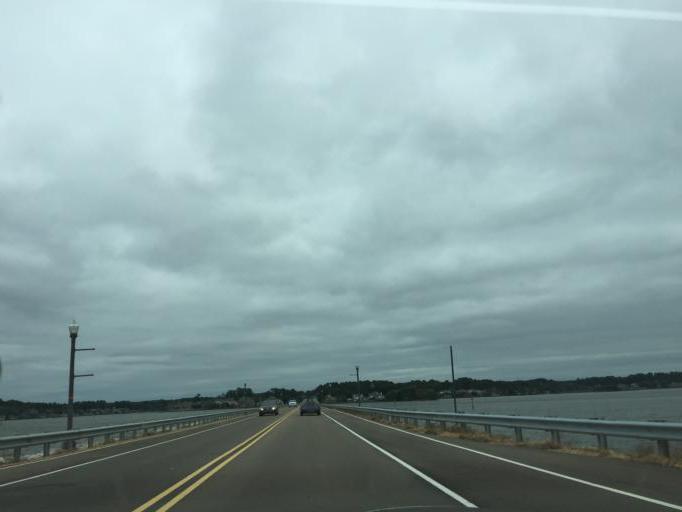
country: US
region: Mississippi
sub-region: Madison County
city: Madison
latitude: 32.4008
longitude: -90.0203
